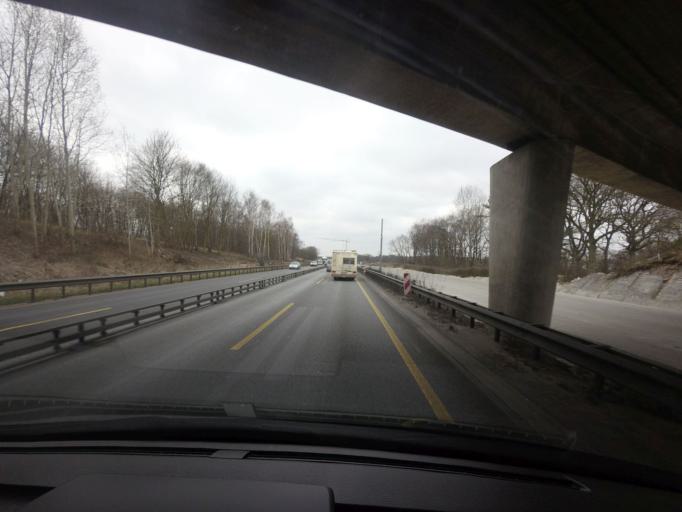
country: DE
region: Schleswig-Holstein
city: Bonningstedt
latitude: 53.6616
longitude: 9.9342
